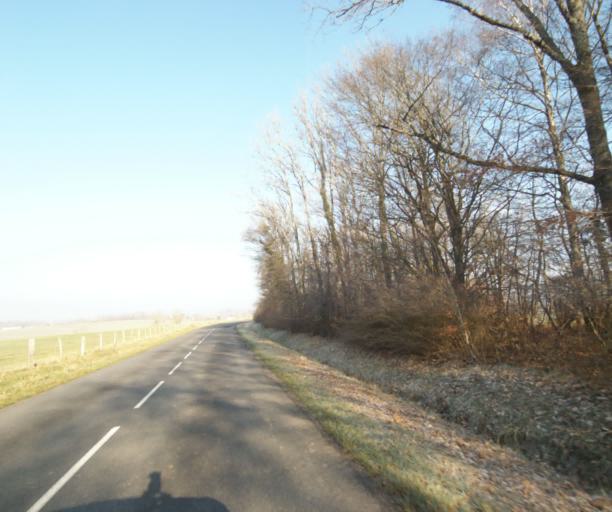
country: FR
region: Champagne-Ardenne
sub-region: Departement de la Haute-Marne
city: Wassy
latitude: 48.4842
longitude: 4.9359
